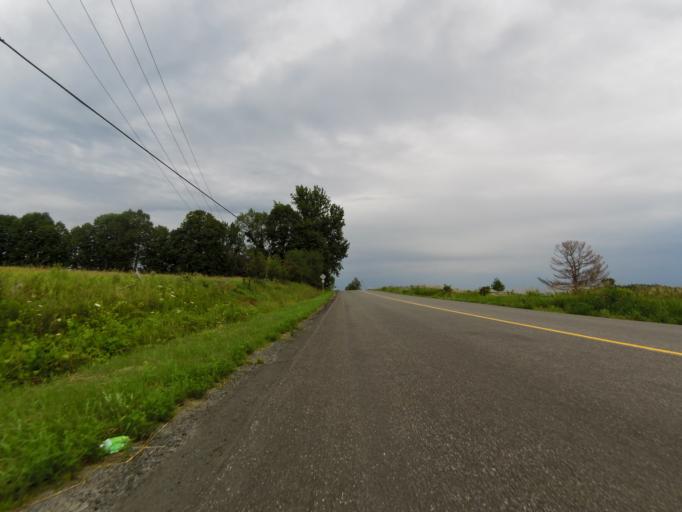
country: CA
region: Ontario
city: Perth
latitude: 45.0816
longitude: -76.3991
